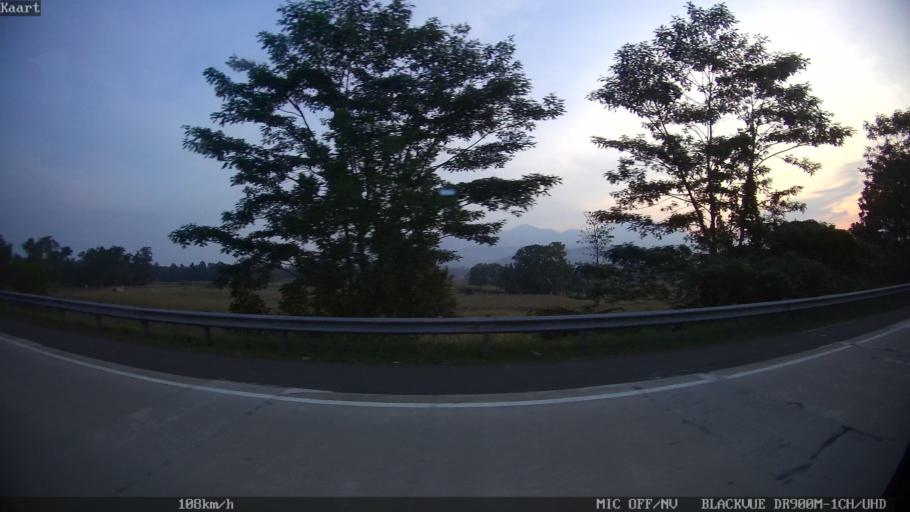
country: ID
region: Lampung
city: Pasuruan
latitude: -5.7424
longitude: 105.6952
